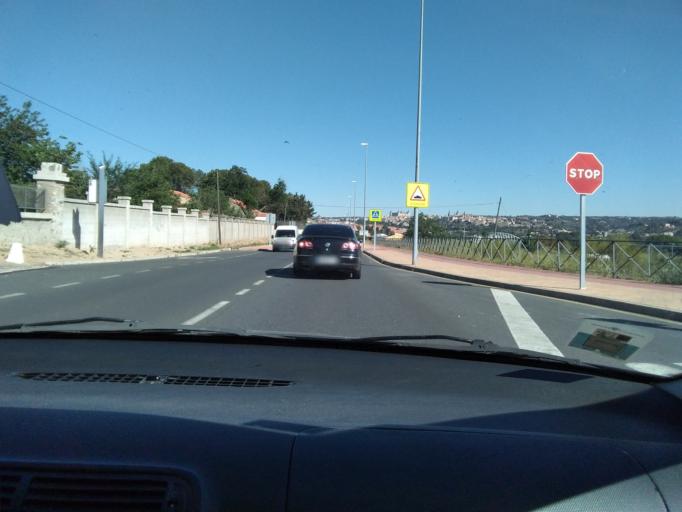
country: ES
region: Castille-La Mancha
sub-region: Province of Toledo
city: Toledo
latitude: 39.8808
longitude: -4.0505
